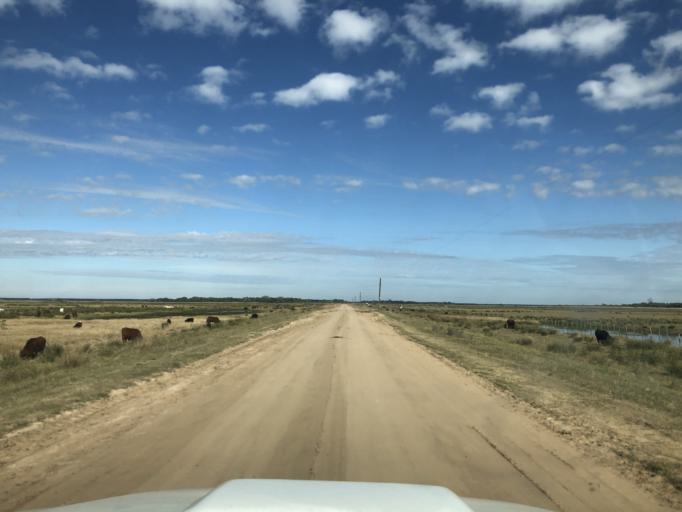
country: AR
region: Corrientes
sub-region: Departamento de Concepcion
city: Concepcion
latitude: -28.4745
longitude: -58.0198
